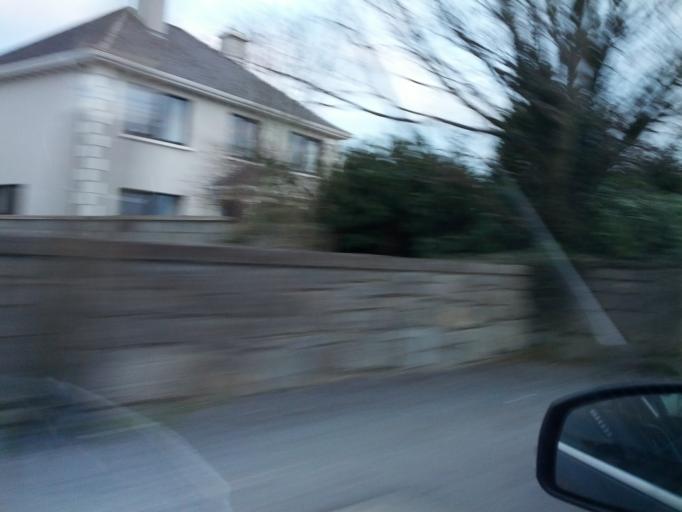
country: IE
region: Connaught
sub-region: County Galway
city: Athenry
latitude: 53.3070
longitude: -8.7521
